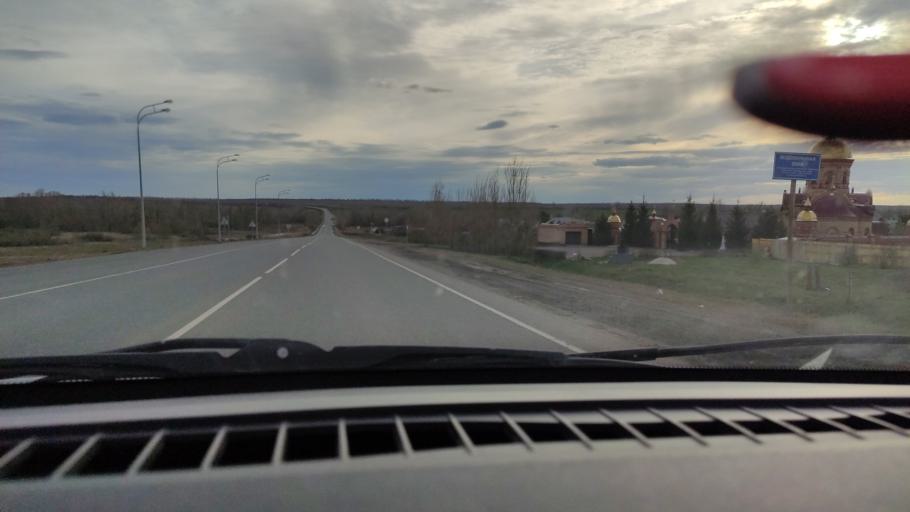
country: RU
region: Orenburg
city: Tatarskaya Kargala
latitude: 52.0261
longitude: 55.2273
